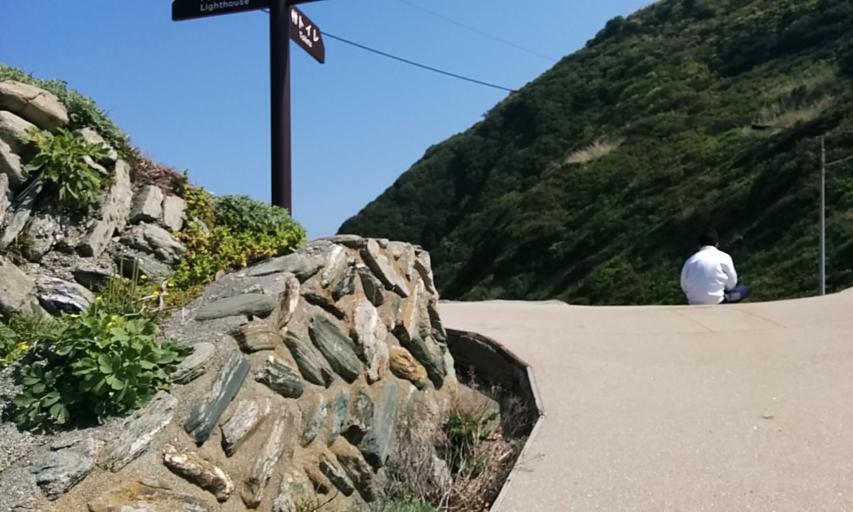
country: JP
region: Oita
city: Tsukumiura
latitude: 33.3451
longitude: 132.0182
